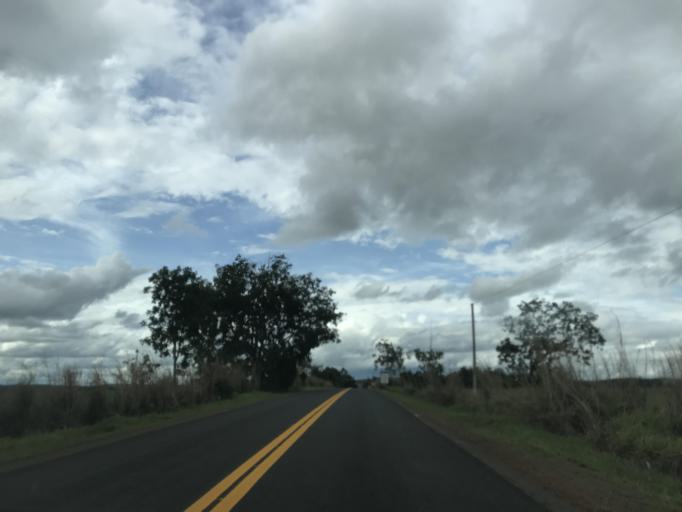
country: BR
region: Goias
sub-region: Bela Vista De Goias
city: Bela Vista de Goias
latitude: -17.0759
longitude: -48.6576
